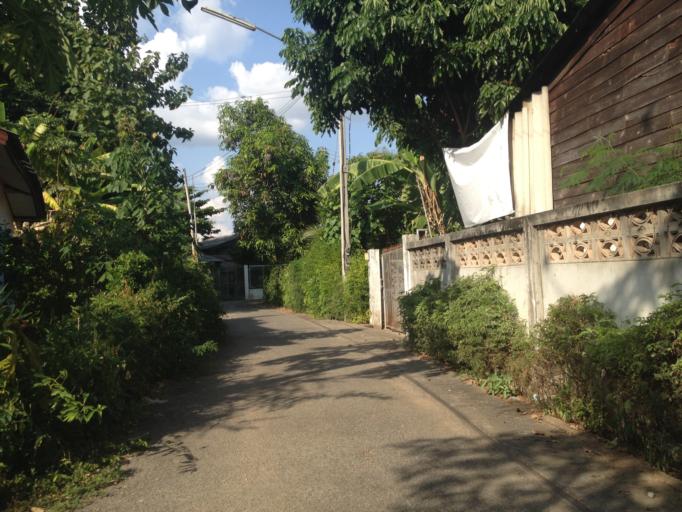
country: TH
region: Chiang Mai
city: Hang Dong
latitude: 18.7027
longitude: 98.9299
